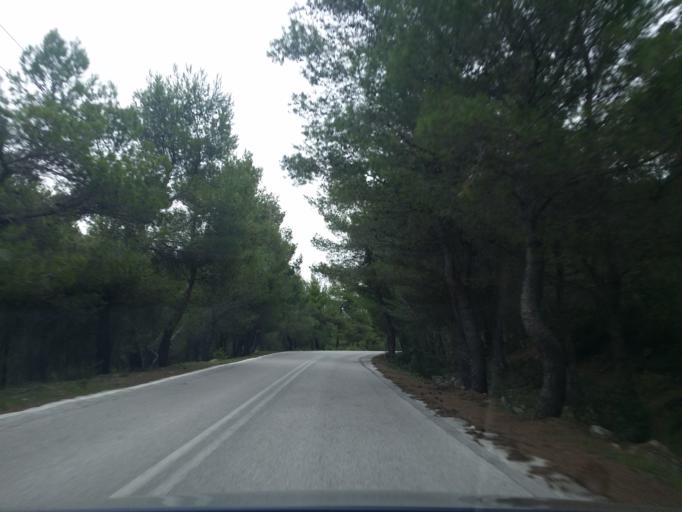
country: GR
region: Attica
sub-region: Nomarchia Dytikis Attikis
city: Vilia
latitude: 38.1435
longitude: 23.2876
